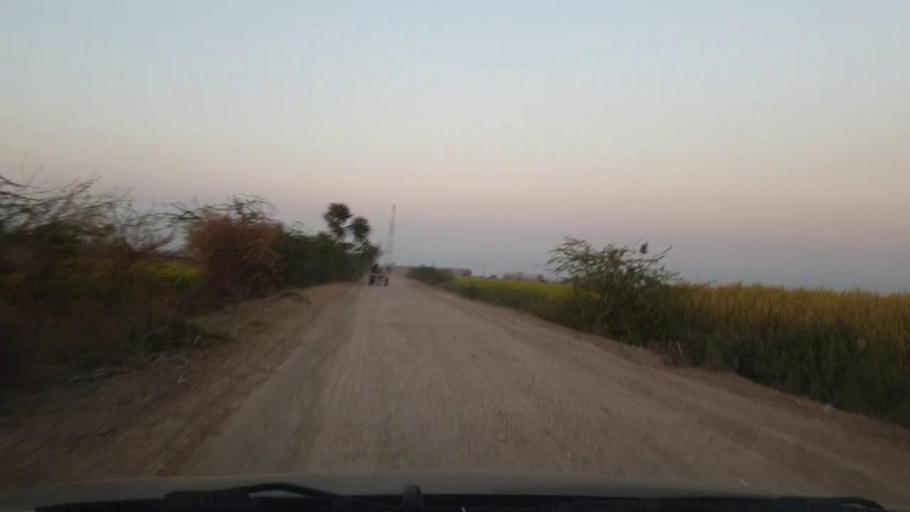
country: PK
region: Sindh
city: Jhol
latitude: 25.9479
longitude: 68.9752
